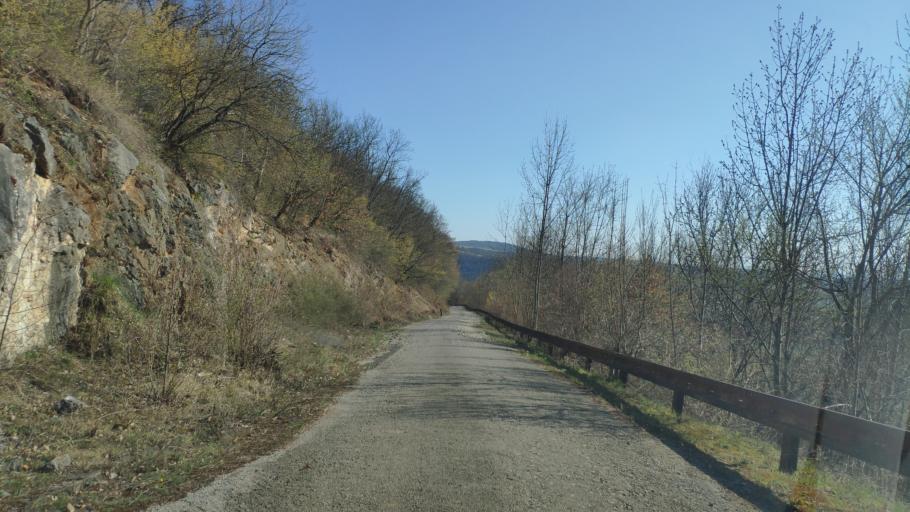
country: SK
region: Kosicky
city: Roznava
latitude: 48.5642
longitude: 20.4025
